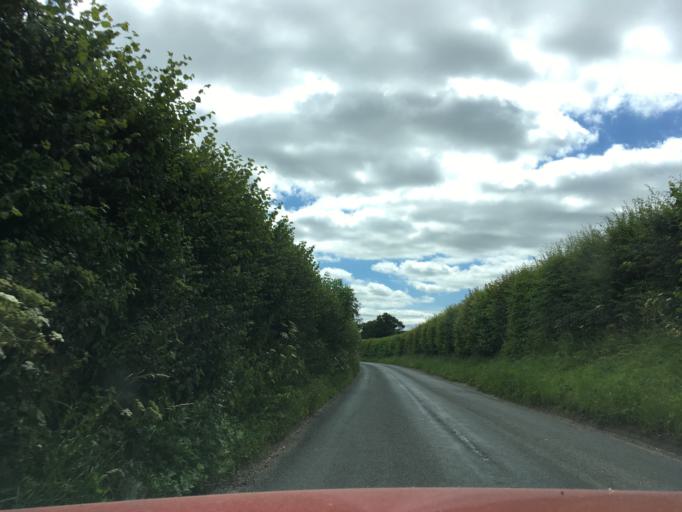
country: GB
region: England
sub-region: West Berkshire
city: Welford
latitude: 51.4317
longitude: -1.3835
